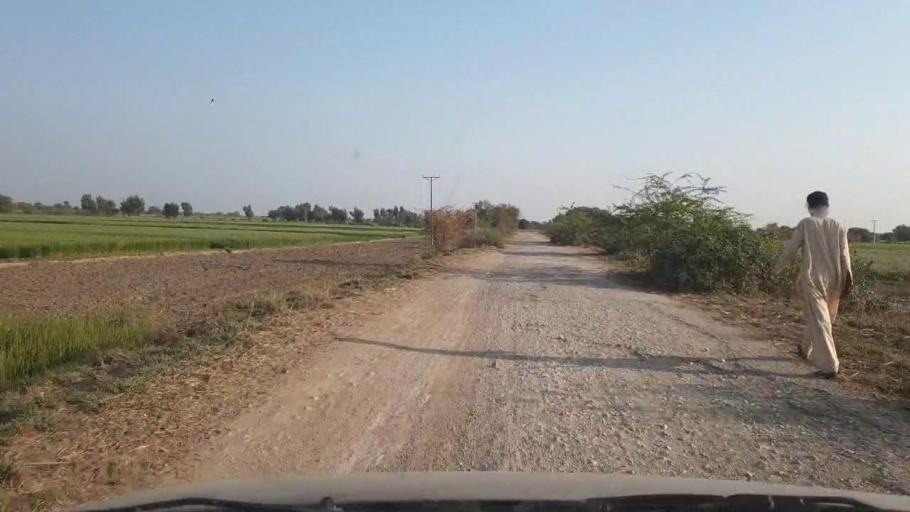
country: PK
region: Sindh
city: Samaro
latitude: 25.2774
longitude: 69.3615
